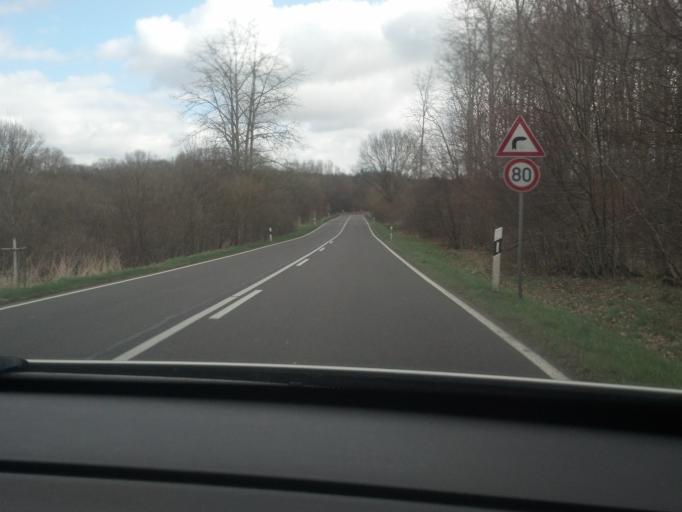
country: DE
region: Mecklenburg-Vorpommern
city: Rechlin
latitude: 53.3133
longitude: 12.7628
